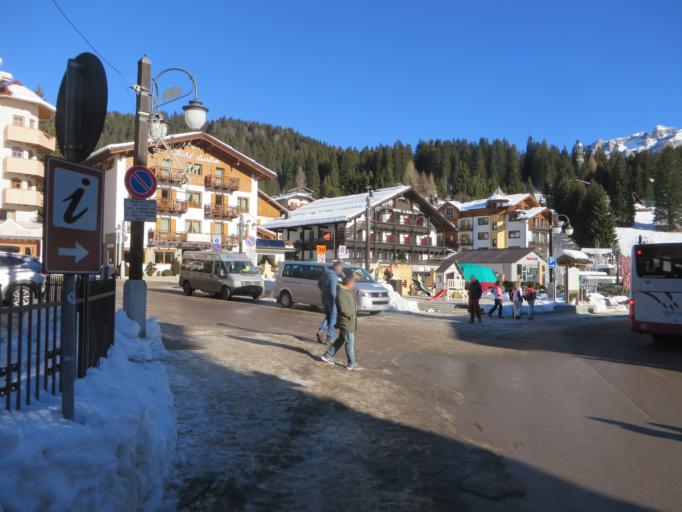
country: IT
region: Trentino-Alto Adige
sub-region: Provincia di Trento
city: Mezzana
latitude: 46.2319
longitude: 10.8260
